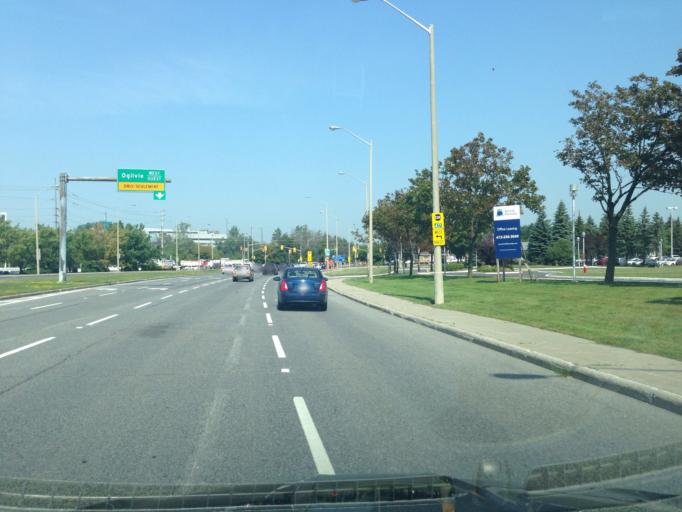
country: CA
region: Ontario
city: Ottawa
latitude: 45.4337
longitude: -75.6076
